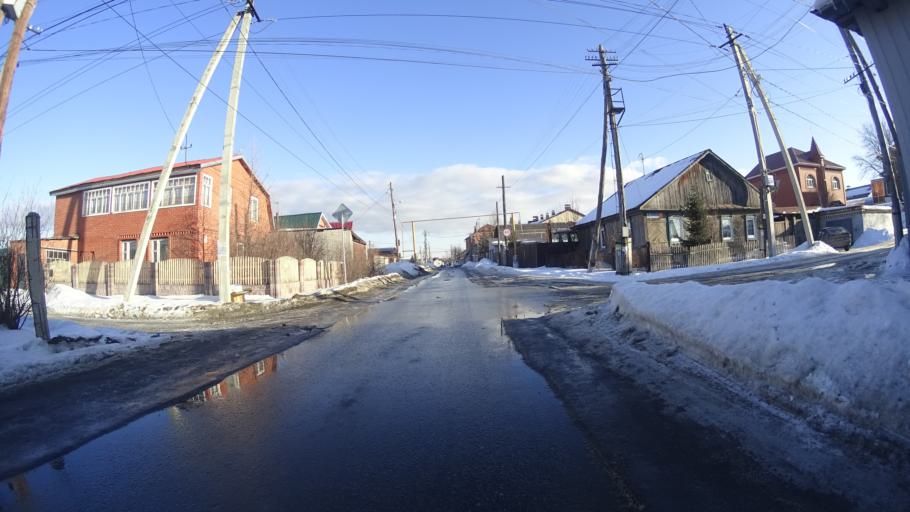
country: RU
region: Chelyabinsk
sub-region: Gorod Chelyabinsk
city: Chelyabinsk
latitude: 55.1554
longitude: 61.3064
